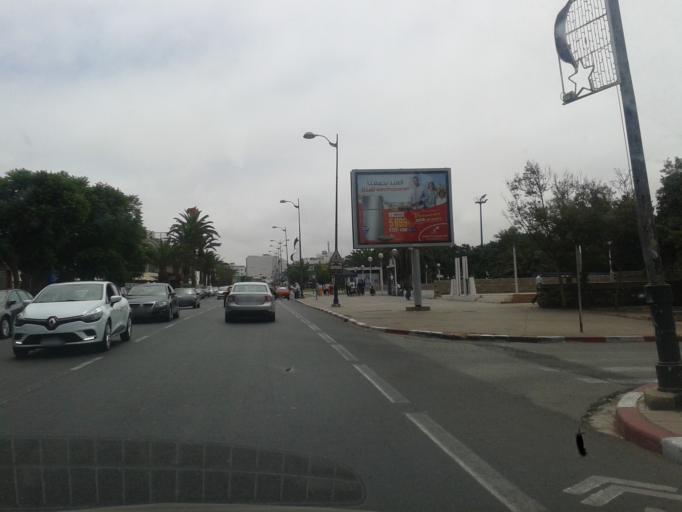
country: MA
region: Souss-Massa-Draa
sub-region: Agadir-Ida-ou-Tnan
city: Agadir
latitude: 30.4216
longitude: -9.6010
